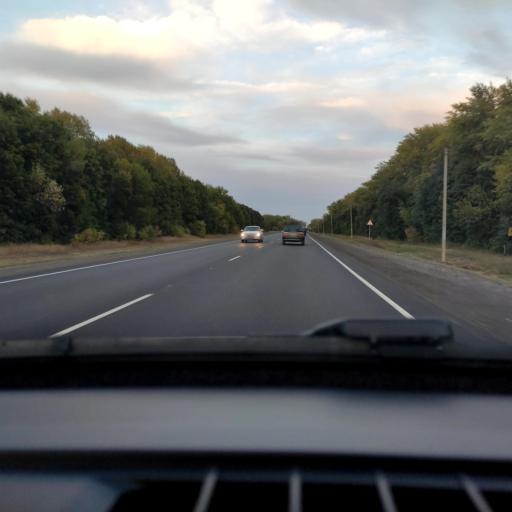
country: RU
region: Voronezj
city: Panino
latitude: 51.4893
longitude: 40.2297
